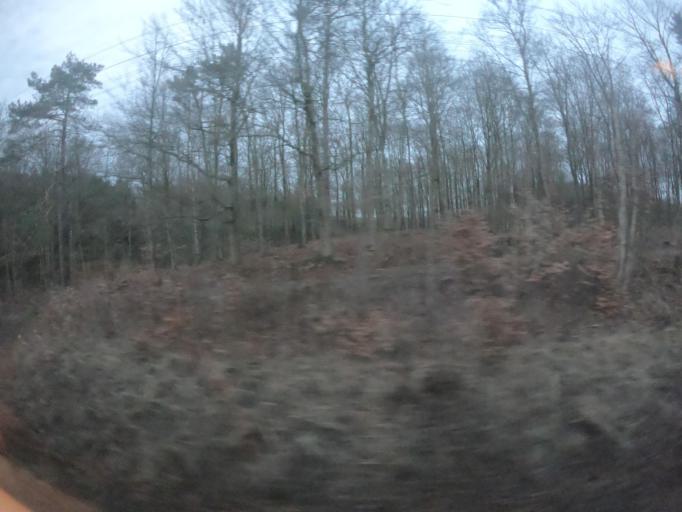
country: PL
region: West Pomeranian Voivodeship
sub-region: Powiat drawski
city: Wierzchowo
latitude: 53.5275
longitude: 16.1005
